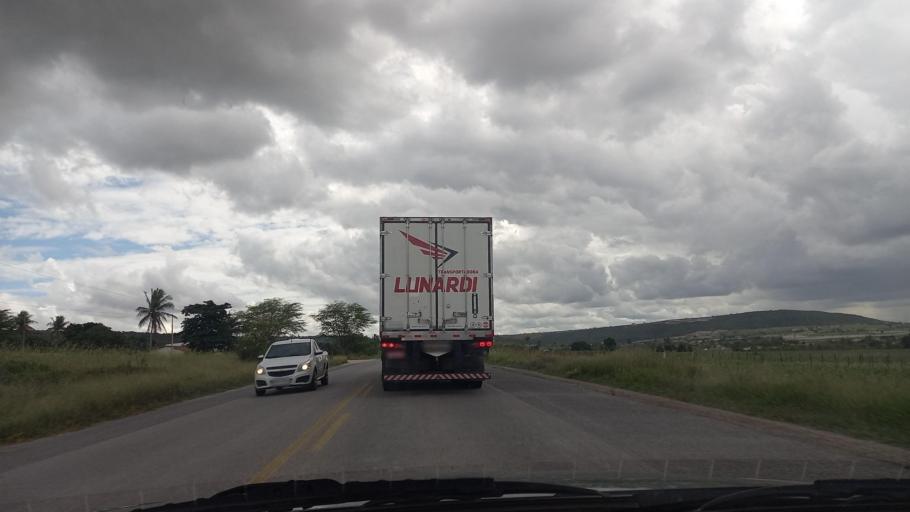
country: BR
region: Pernambuco
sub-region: Lajedo
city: Lajedo
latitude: -8.6674
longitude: -36.3704
